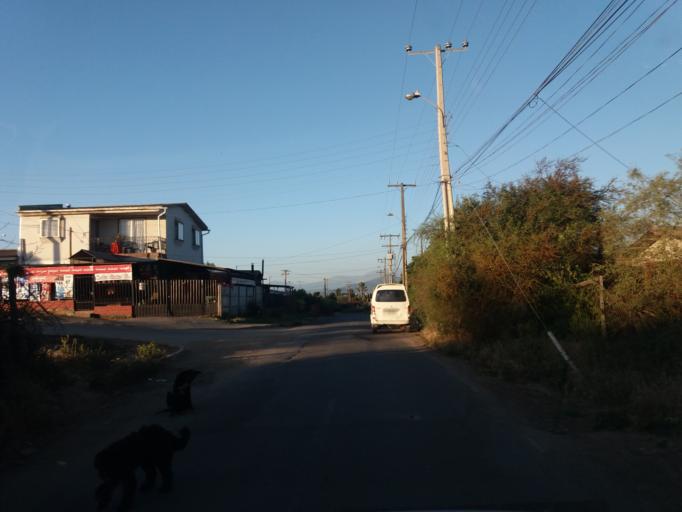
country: CL
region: Valparaiso
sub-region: Provincia de Quillota
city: Quillota
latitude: -32.9448
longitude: -71.2713
